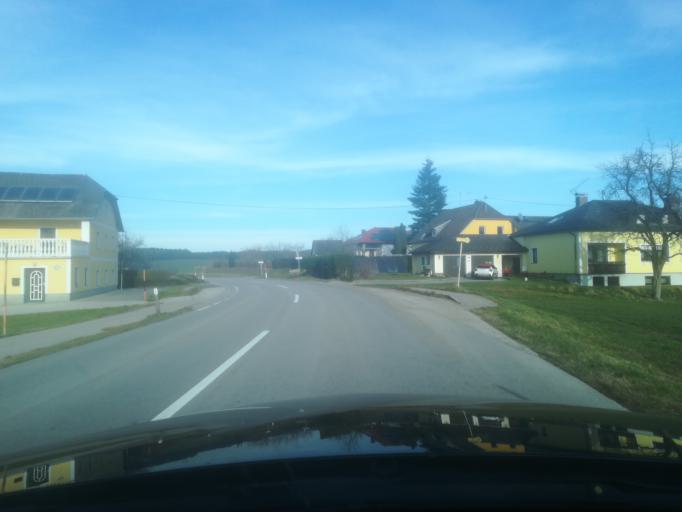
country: AT
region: Upper Austria
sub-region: Politischer Bezirk Perg
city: Perg
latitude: 48.3133
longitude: 14.6628
